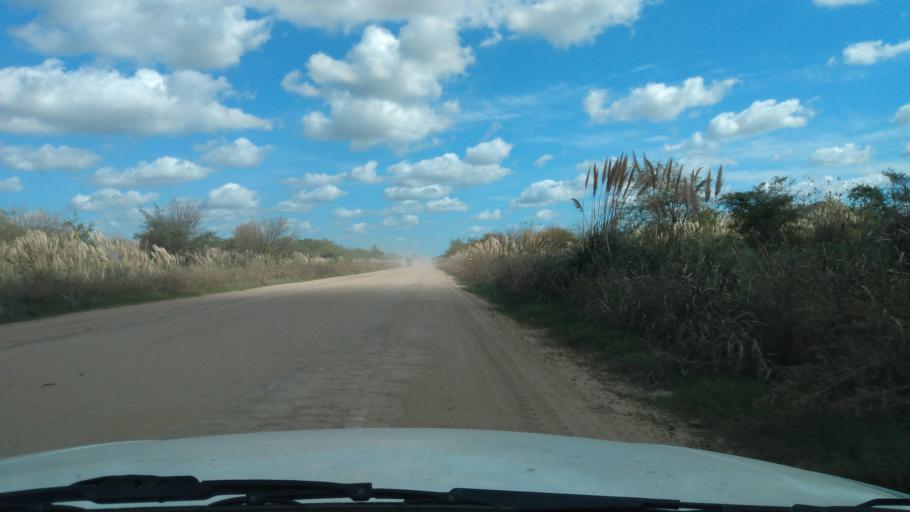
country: AR
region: Buenos Aires
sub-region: Partido de Navarro
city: Navarro
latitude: -34.9982
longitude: -59.3225
